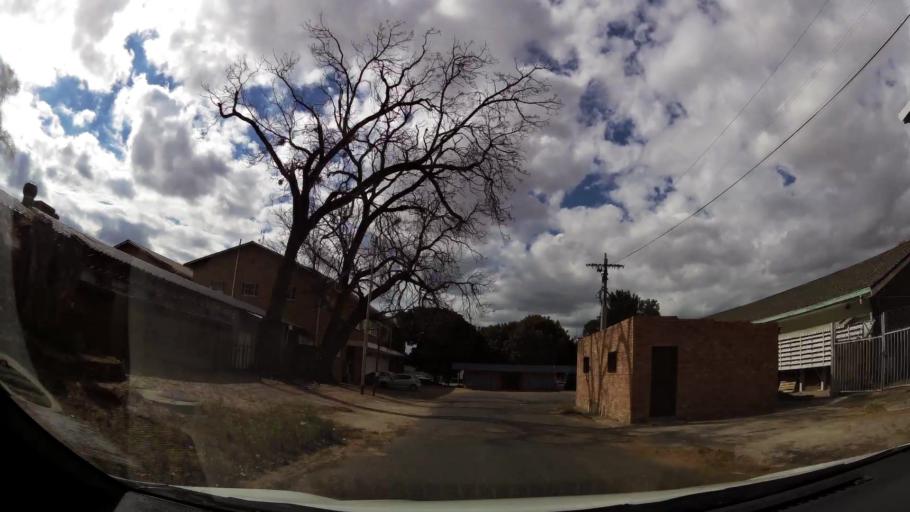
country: ZA
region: Limpopo
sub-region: Waterberg District Municipality
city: Modimolle
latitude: -24.7041
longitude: 28.4084
